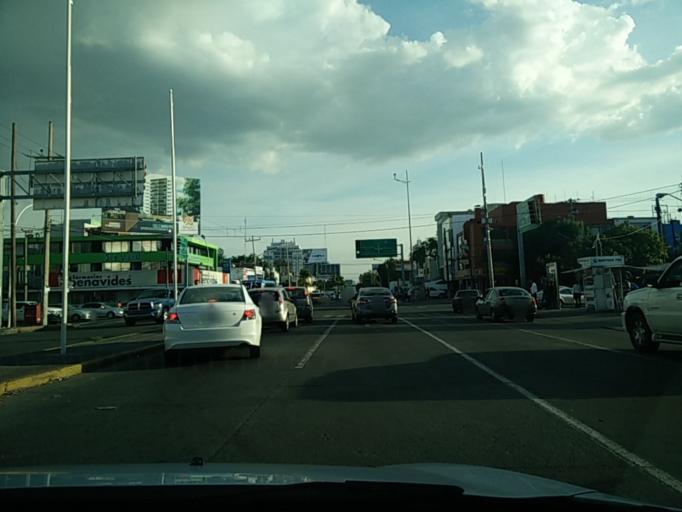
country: MX
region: Jalisco
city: Guadalajara
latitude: 20.6797
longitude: -103.3737
